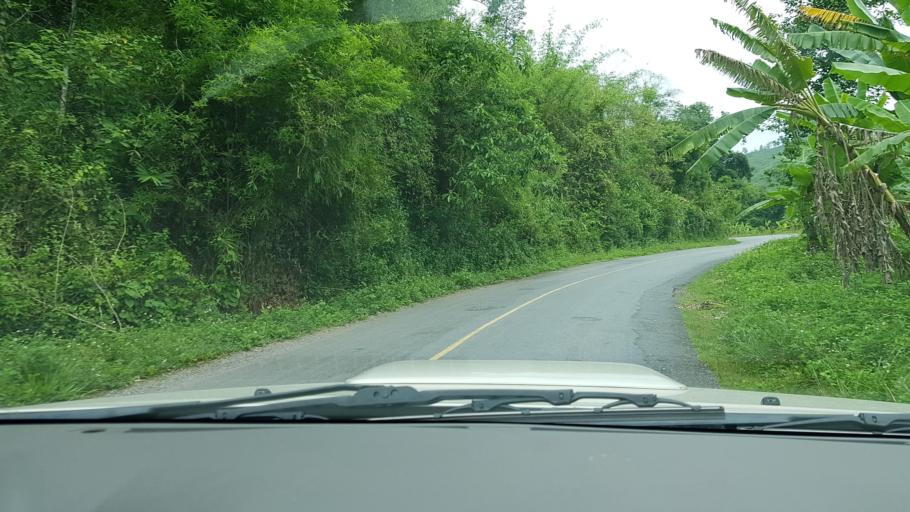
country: LA
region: Loungnamtha
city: Muang Nale
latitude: 20.3746
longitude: 101.7334
